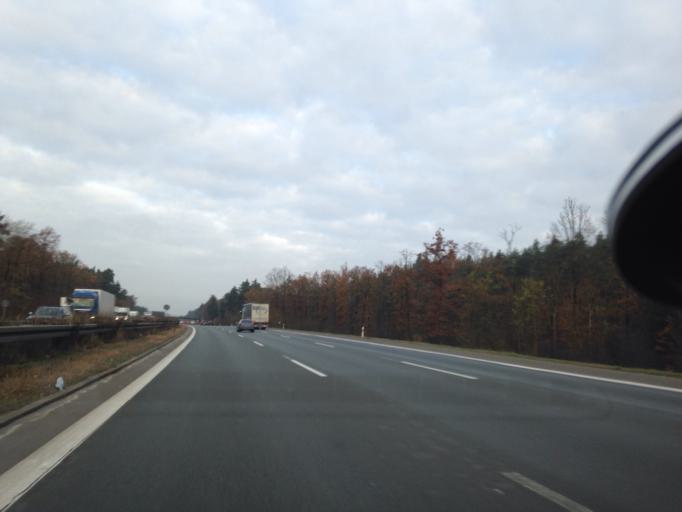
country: DE
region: Bavaria
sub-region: Regierungsbezirk Mittelfranken
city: Schwaig
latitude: 49.4831
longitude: 11.1689
